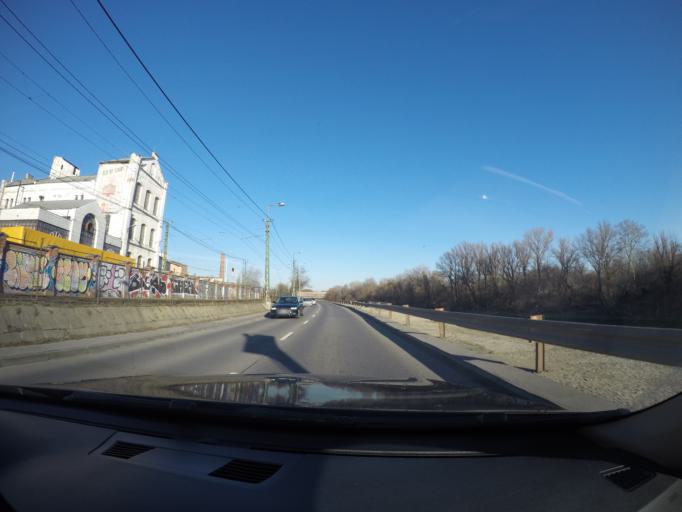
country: HU
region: Budapest
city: Budapest III. keruelet
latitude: 47.5471
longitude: 19.0476
